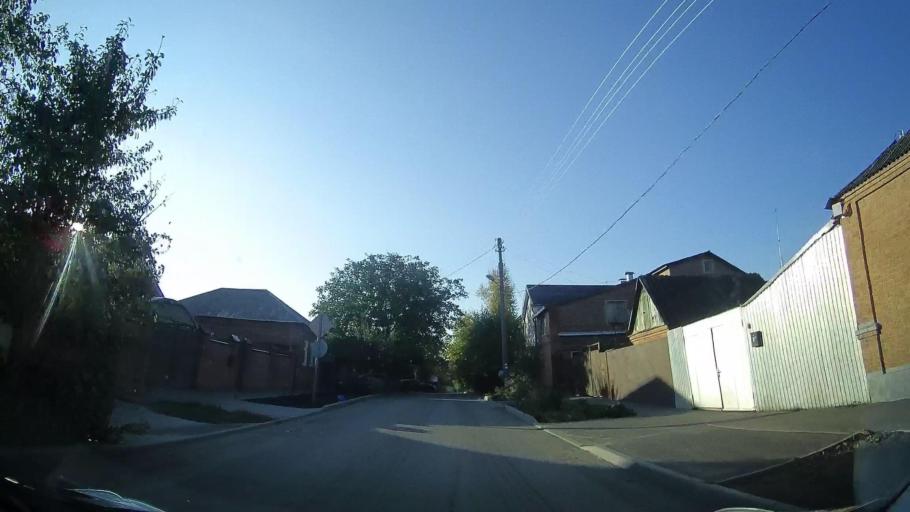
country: RU
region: Rostov
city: Severnyy
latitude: 47.2707
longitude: 39.6722
